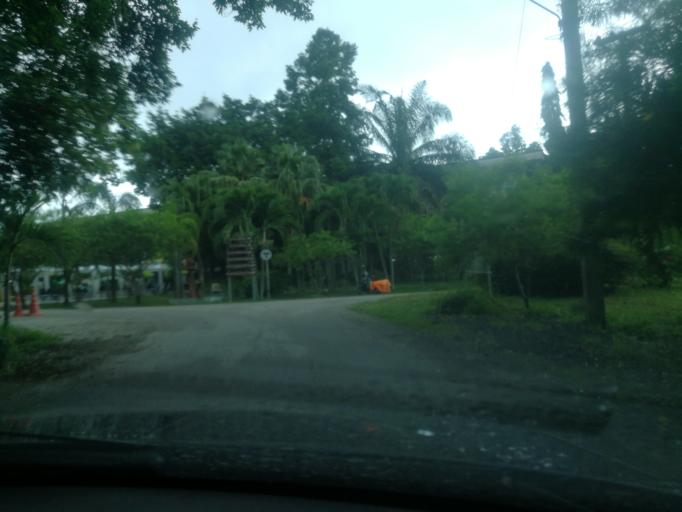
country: TH
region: Chiang Mai
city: San Pa Tong
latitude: 18.6474
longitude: 98.8502
